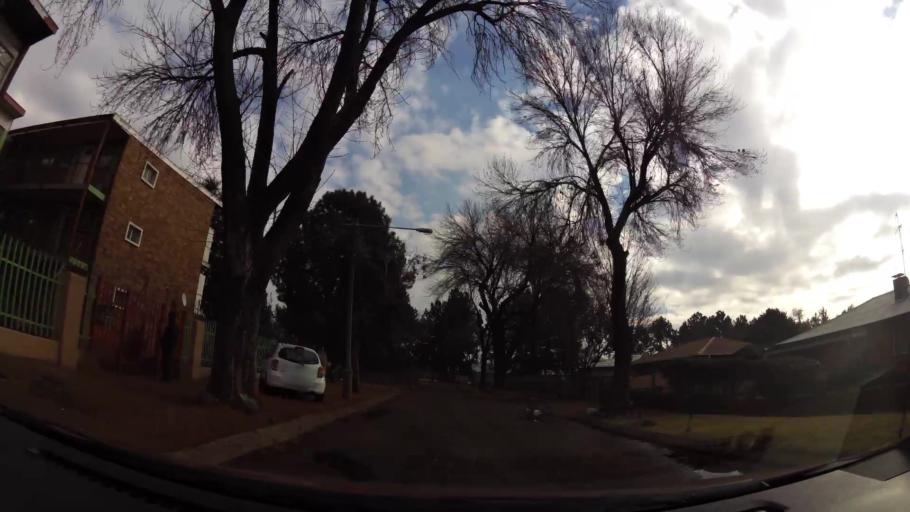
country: ZA
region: Gauteng
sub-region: Sedibeng District Municipality
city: Vanderbijlpark
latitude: -26.7018
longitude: 27.8273
